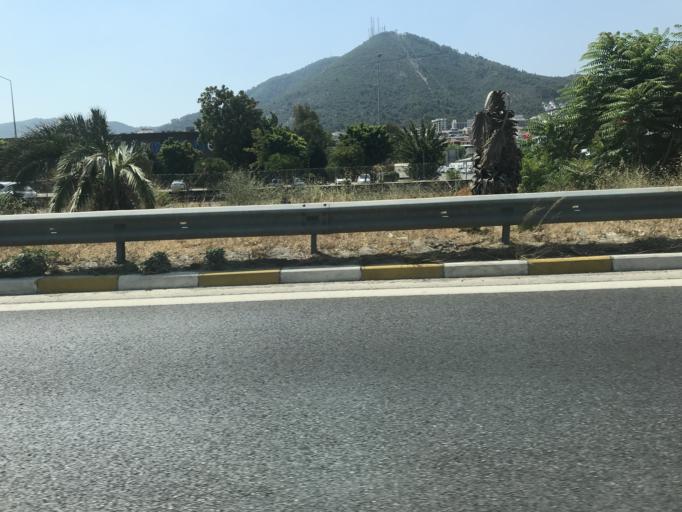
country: TR
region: Izmir
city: Karsiyaka
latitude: 38.3963
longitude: 27.0479
